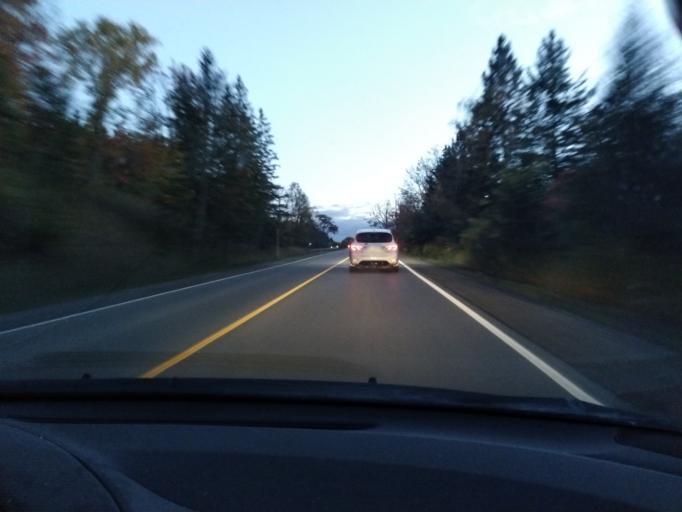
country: CA
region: Ontario
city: Bradford West Gwillimbury
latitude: 44.1562
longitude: -79.6539
